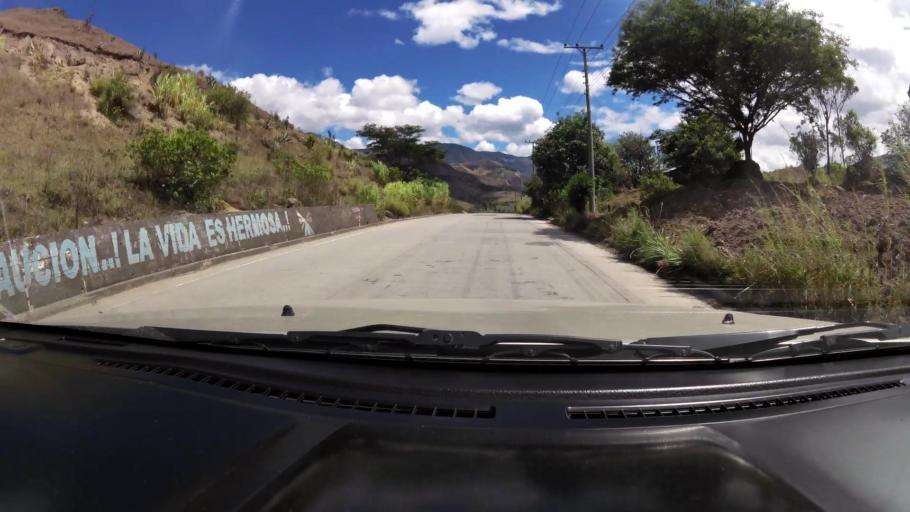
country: EC
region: Azuay
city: Cuenca
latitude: -3.1923
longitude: -79.1727
